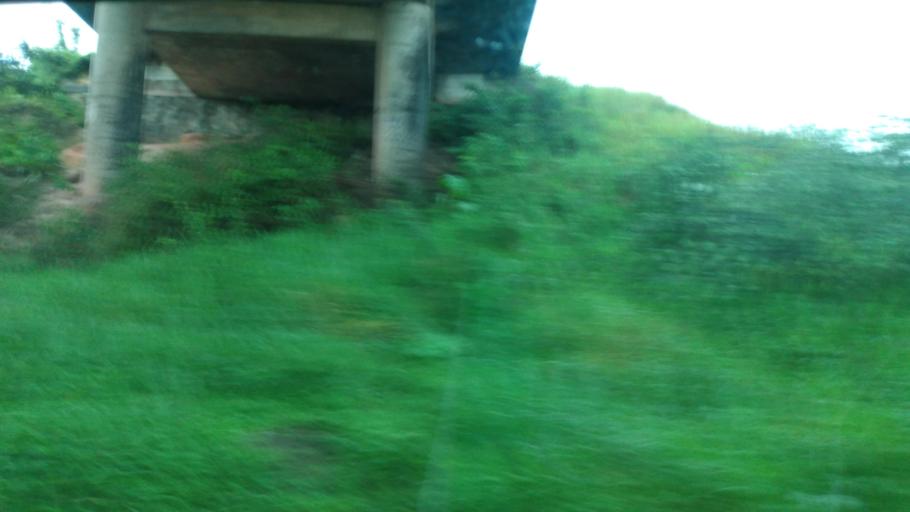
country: BR
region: Pernambuco
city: Garanhuns
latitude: -8.8769
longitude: -36.5072
